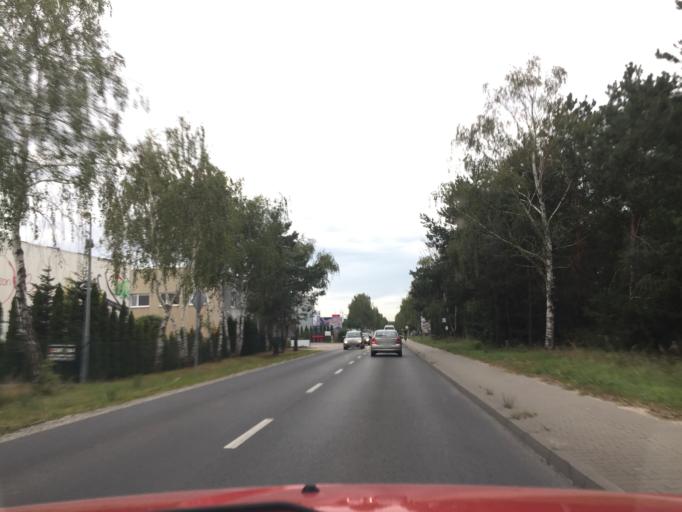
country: PL
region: Greater Poland Voivodeship
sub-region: Powiat poznanski
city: Baranowo
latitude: 52.4061
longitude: 16.7950
